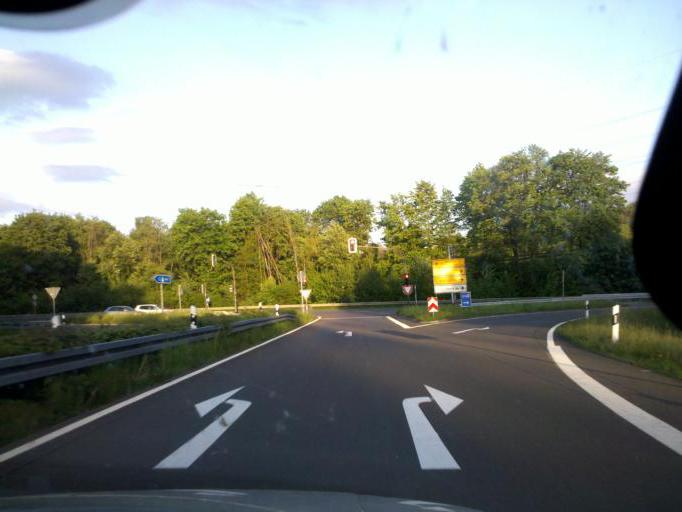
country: DE
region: North Rhine-Westphalia
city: Wiehl
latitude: 50.9738
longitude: 7.5260
